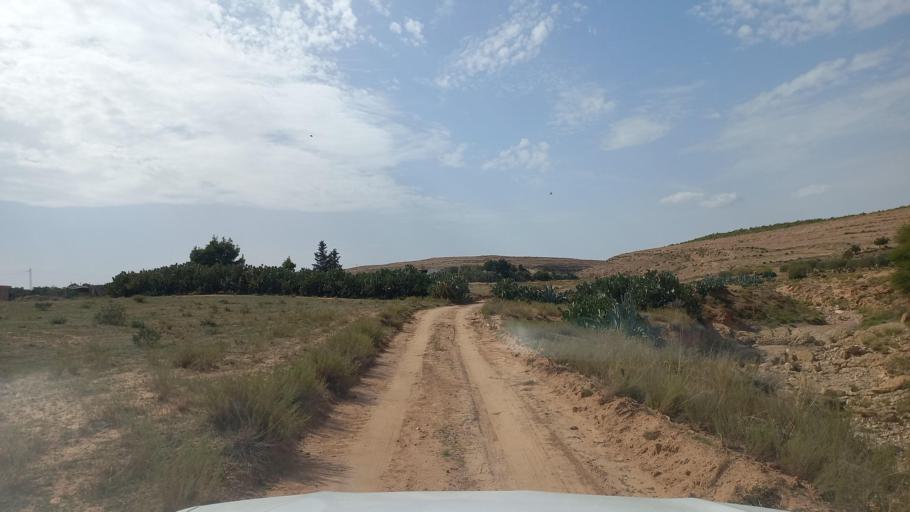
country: TN
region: Al Qasrayn
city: Kasserine
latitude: 35.3649
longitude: 8.8564
